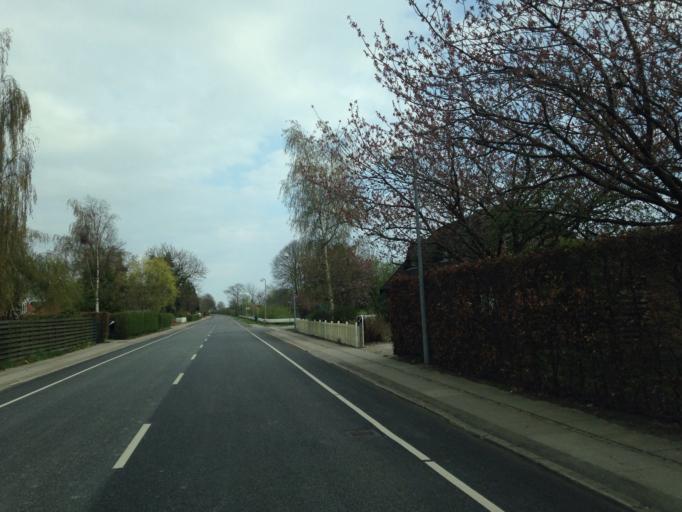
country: DK
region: Capital Region
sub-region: Hoje-Taastrup Kommune
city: Taastrup
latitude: 55.6238
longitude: 12.3057
